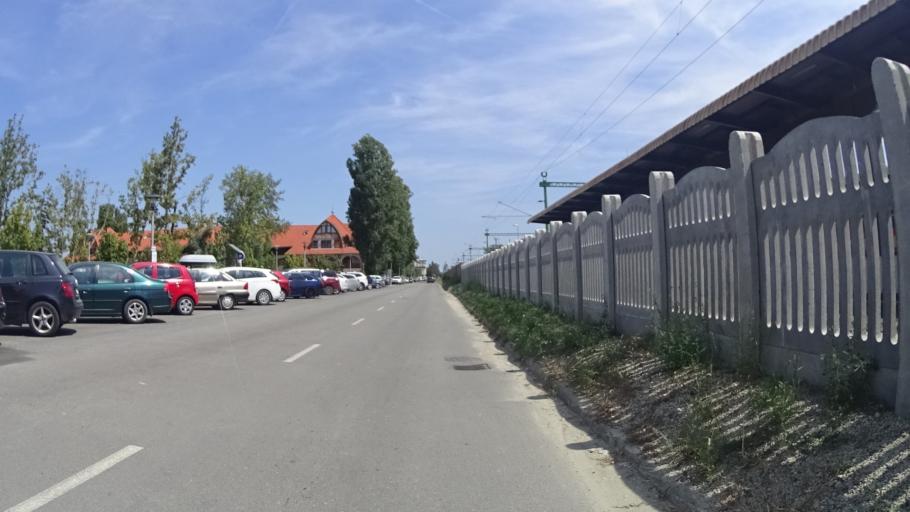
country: HU
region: Somogy
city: Fonyod
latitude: 46.7503
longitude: 17.5578
